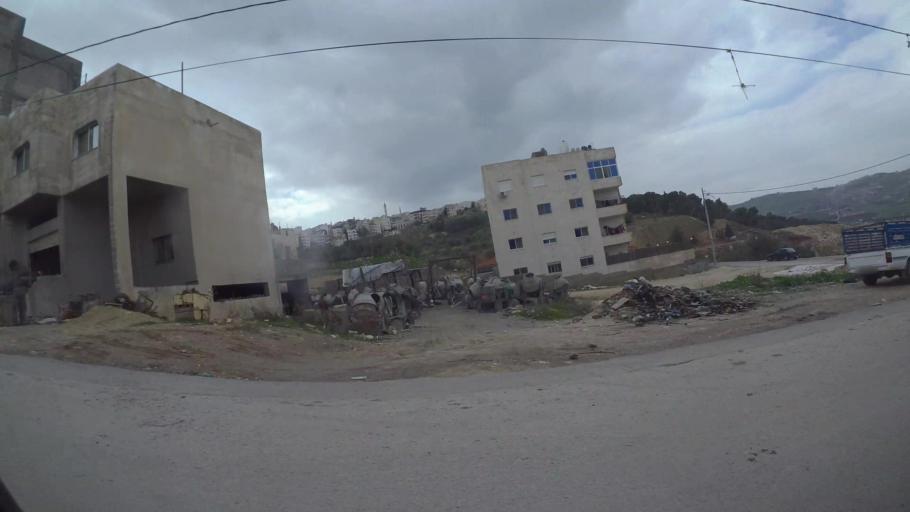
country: JO
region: Amman
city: Al Jubayhah
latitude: 32.0417
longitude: 35.8318
